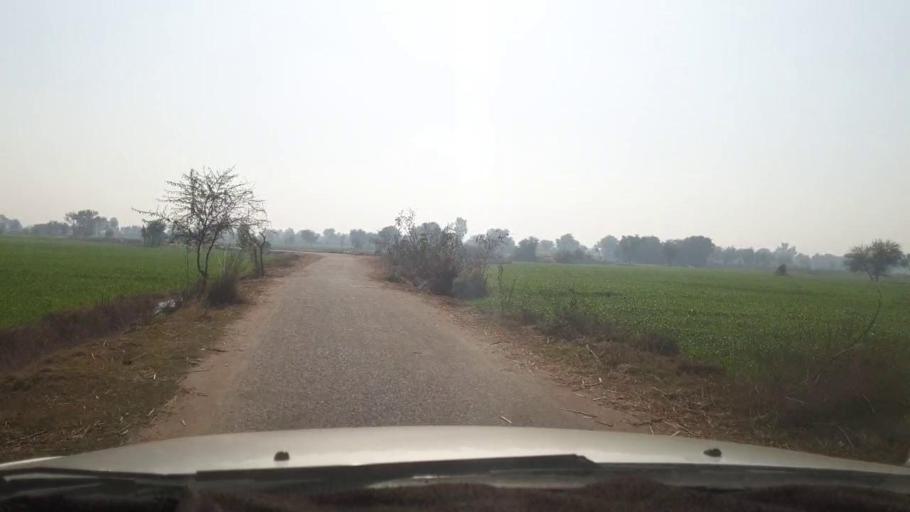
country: PK
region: Sindh
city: Khanpur
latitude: 27.7409
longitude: 69.5053
